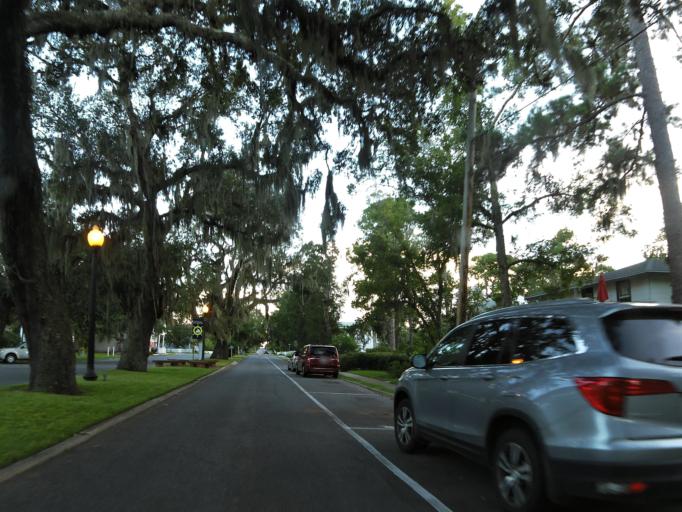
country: US
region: Georgia
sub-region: Camden County
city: St. Marys
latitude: 30.7259
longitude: -81.5474
